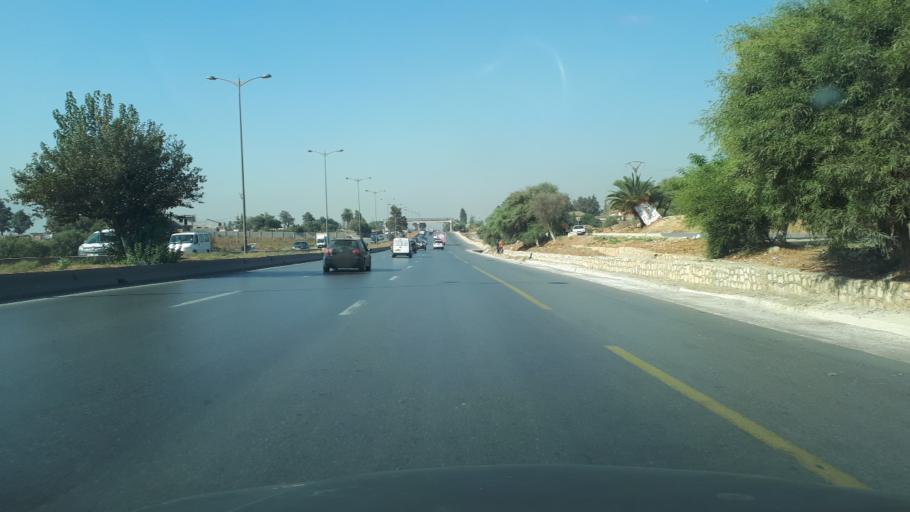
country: DZ
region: Tipaza
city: Saoula
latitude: 36.6622
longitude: 3.0333
